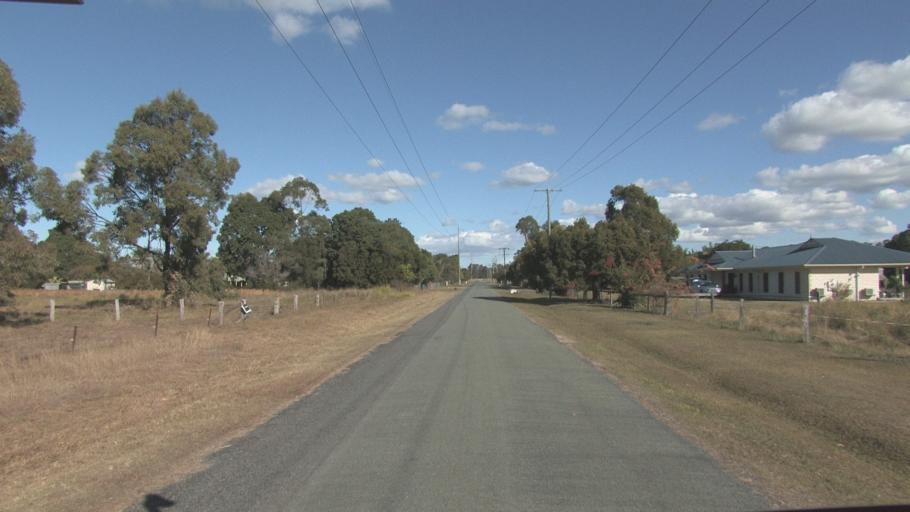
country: AU
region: Queensland
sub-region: Logan
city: Logan Reserve
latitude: -27.7215
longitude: 153.1144
